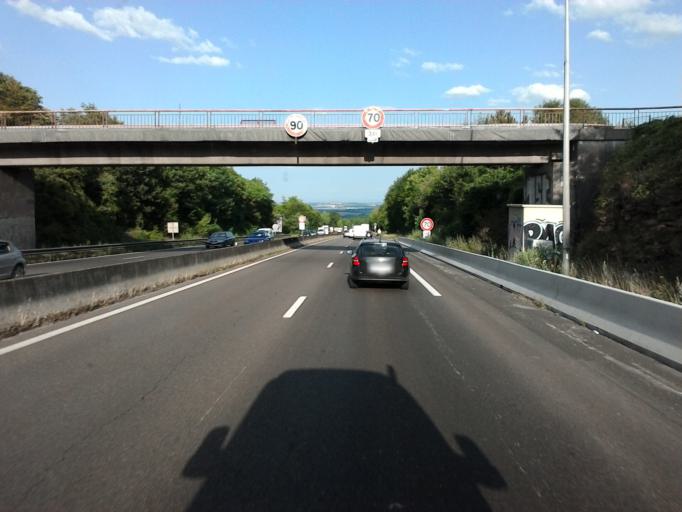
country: FR
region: Lorraine
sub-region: Departement de Meurthe-et-Moselle
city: Ludres
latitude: 48.6428
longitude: 6.1599
